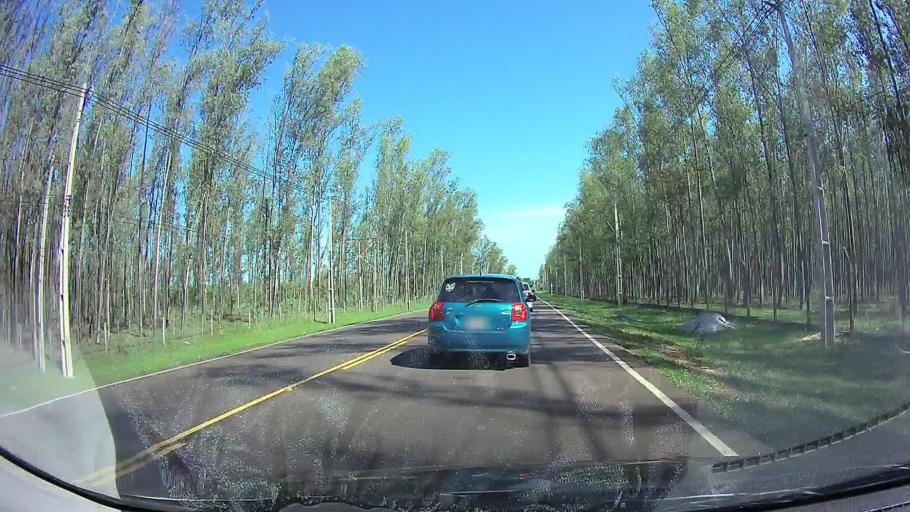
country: PY
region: Central
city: Ypacarai
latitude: -25.3754
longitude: -57.2628
